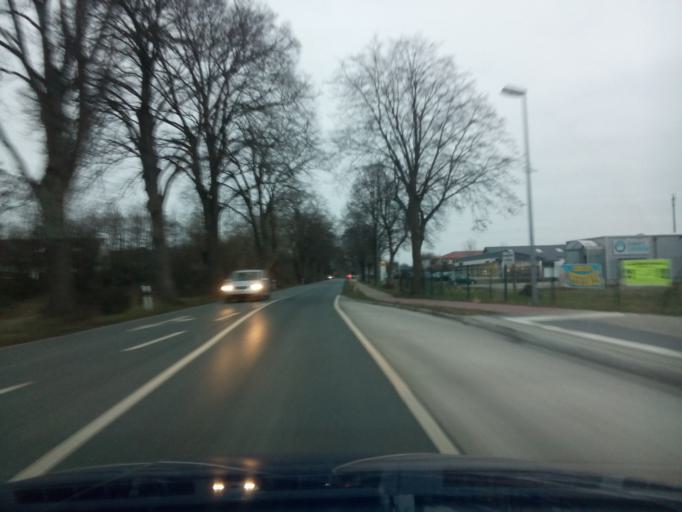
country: DE
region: Lower Saxony
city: Lilienthal
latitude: 53.1579
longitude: 8.9180
